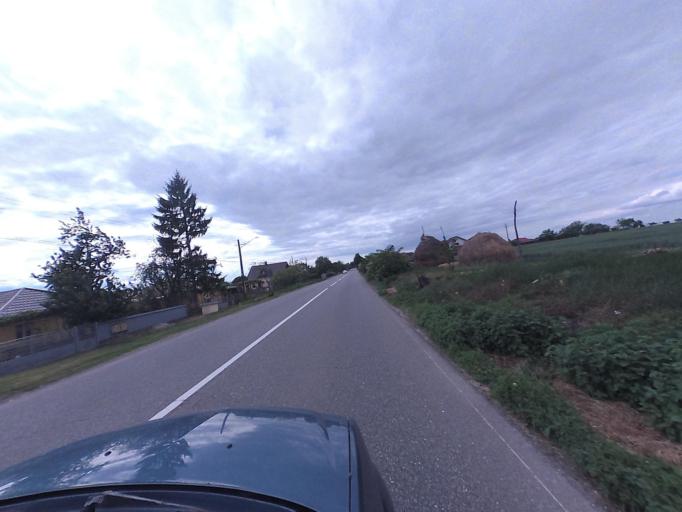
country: RO
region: Neamt
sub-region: Comuna Dulcesti
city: Dulcesti
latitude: 46.9602
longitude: 26.7976
